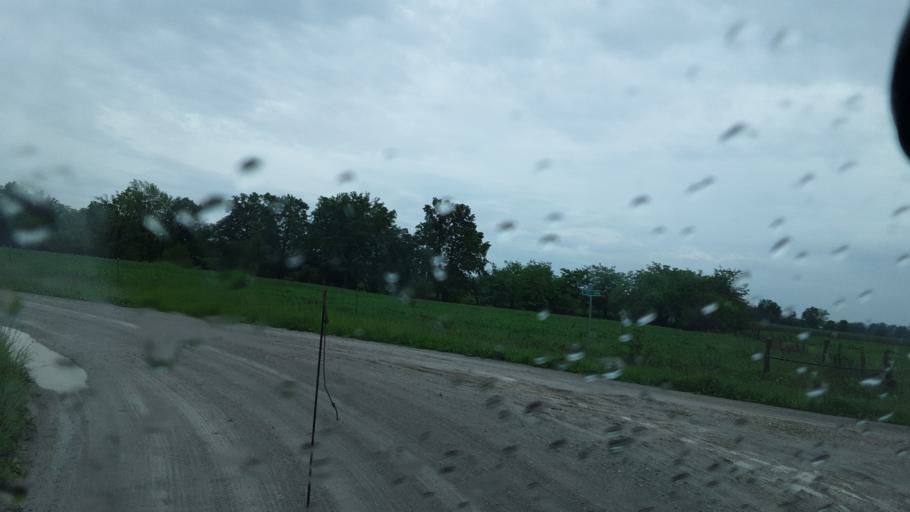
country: US
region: Missouri
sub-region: Randolph County
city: Moberly
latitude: 39.3050
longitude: -92.3054
